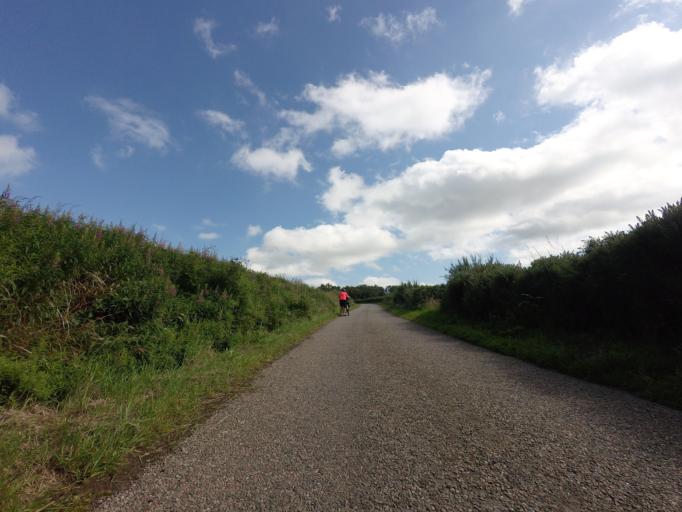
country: GB
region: Scotland
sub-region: Aberdeenshire
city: Banff
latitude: 57.5946
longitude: -2.5099
